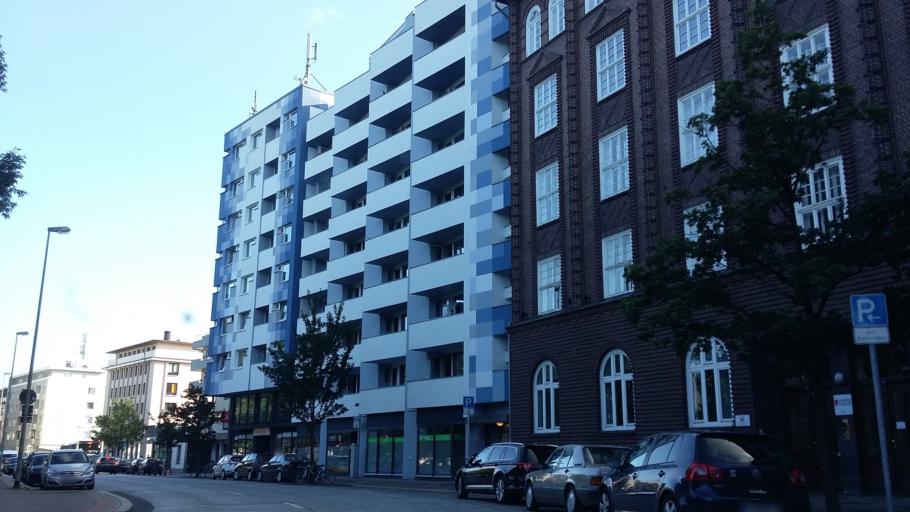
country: DE
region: Bremen
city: Bremerhaven
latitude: 53.5512
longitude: 8.5723
